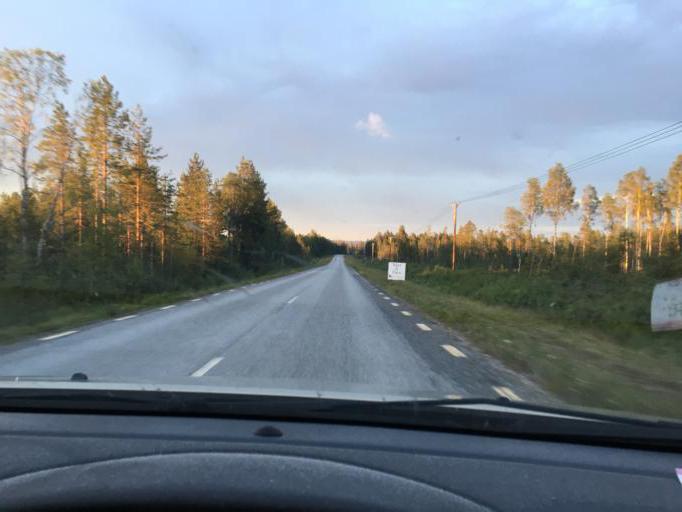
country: SE
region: Norrbotten
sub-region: Kalix Kommun
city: Toere
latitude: 66.0643
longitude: 22.6439
